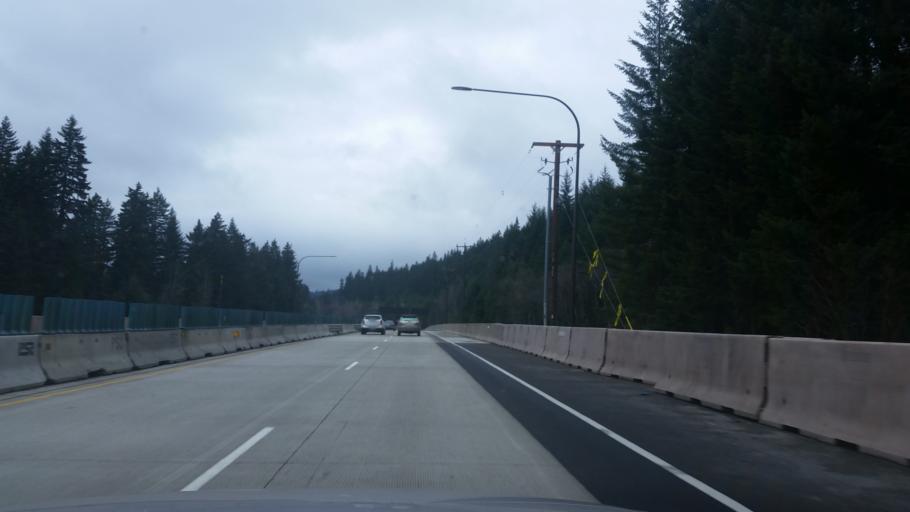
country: US
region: Washington
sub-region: Kittitas County
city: Cle Elum
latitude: 47.3225
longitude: -121.3246
